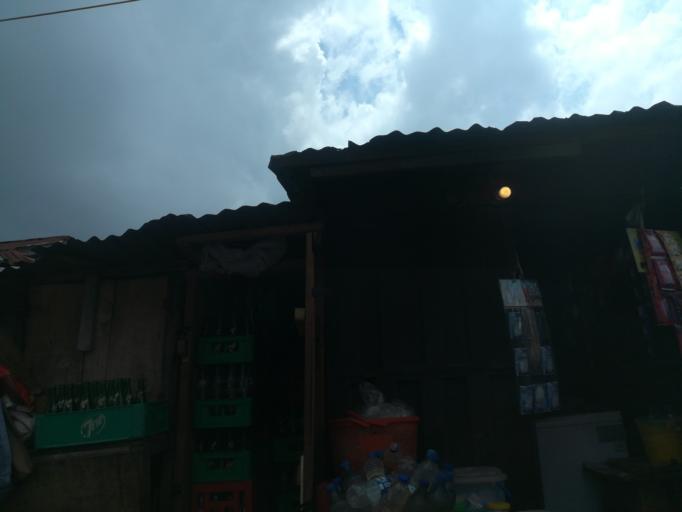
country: NG
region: Lagos
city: Mushin
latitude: 6.5286
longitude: 3.3643
